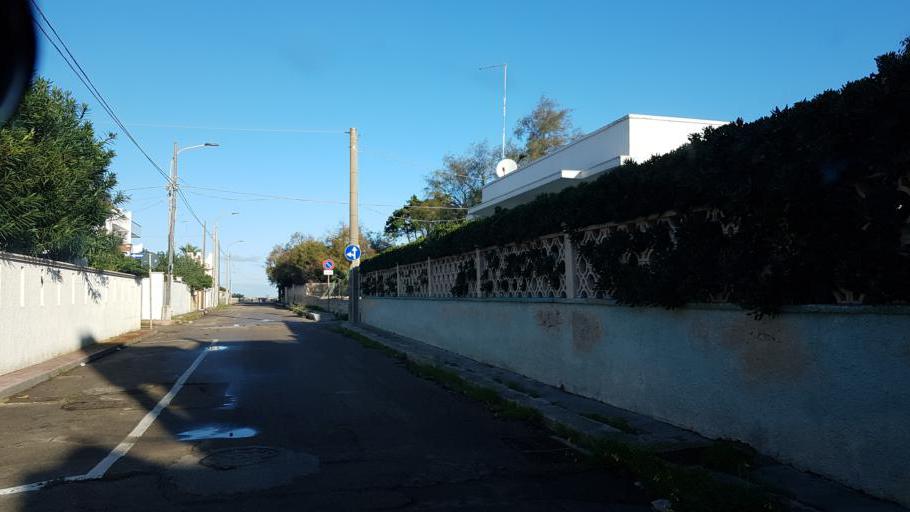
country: IT
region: Apulia
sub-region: Provincia di Brindisi
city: Torchiarolo
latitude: 40.5407
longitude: 18.0660
